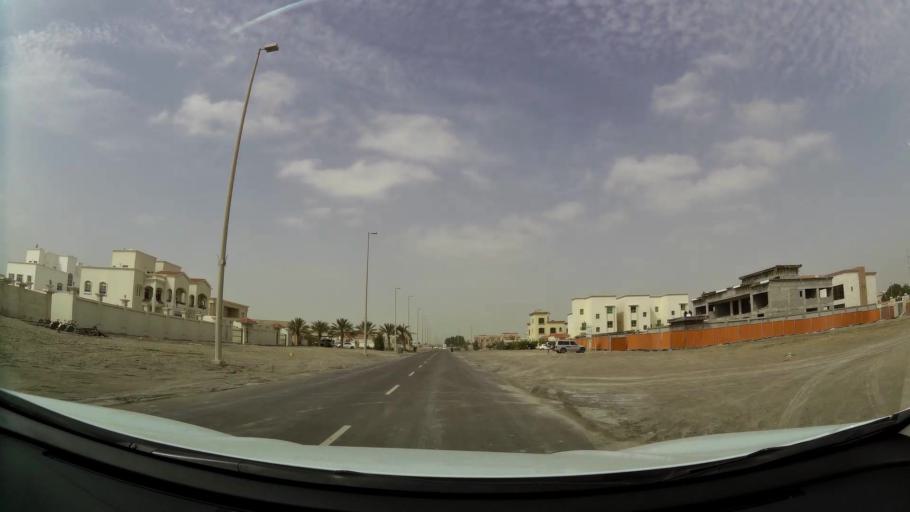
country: AE
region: Abu Dhabi
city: Abu Dhabi
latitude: 24.4028
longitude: 54.5612
